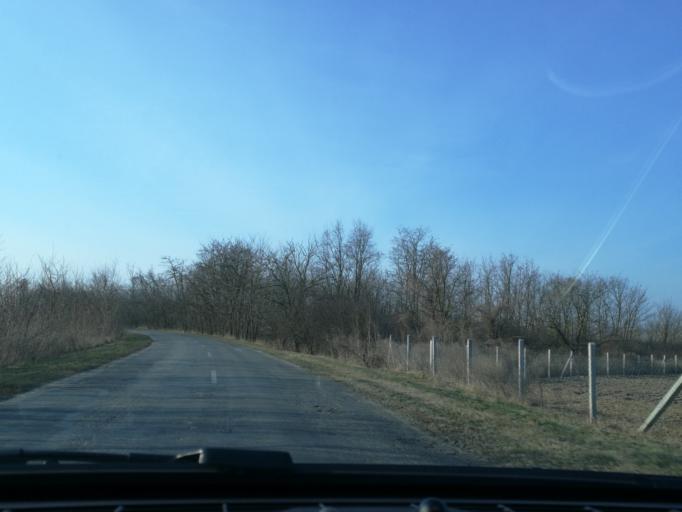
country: HU
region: Szabolcs-Szatmar-Bereg
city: Levelek
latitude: 48.0367
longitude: 21.9746
